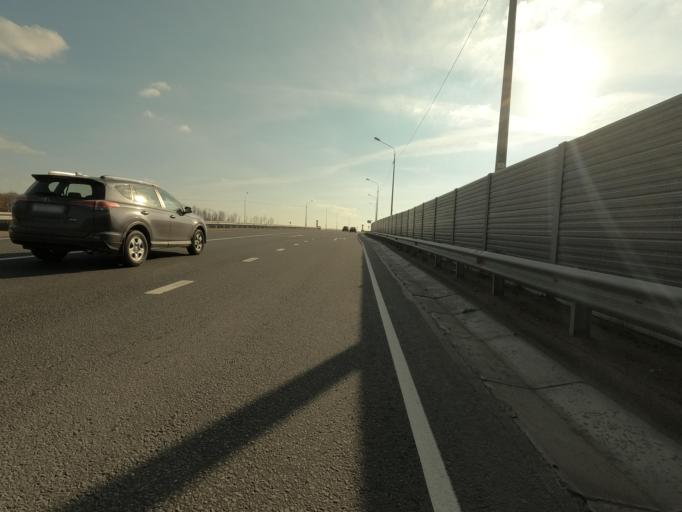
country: RU
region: Leningrad
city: Mga
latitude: 59.7590
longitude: 31.0936
